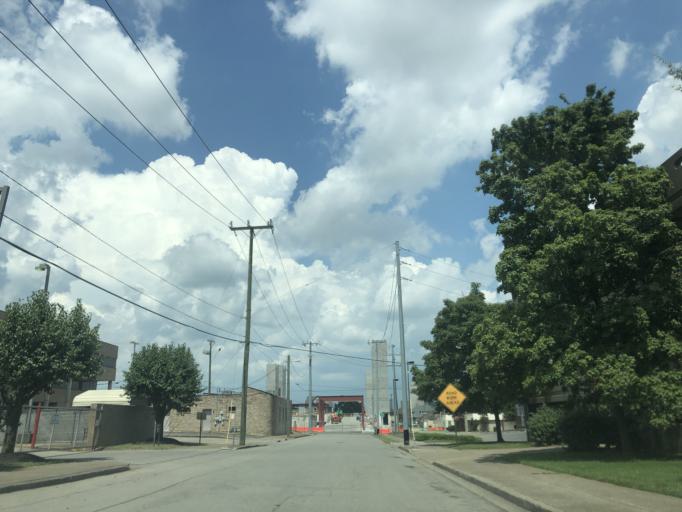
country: US
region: Tennessee
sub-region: Davidson County
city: Nashville
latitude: 36.1552
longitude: -86.8078
